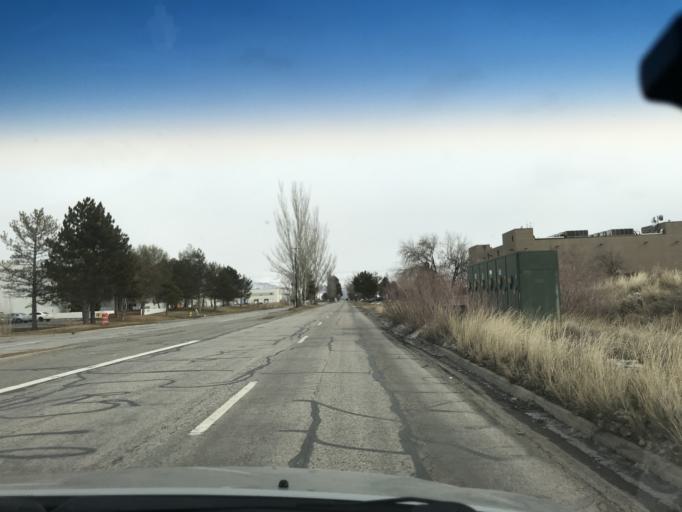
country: US
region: Utah
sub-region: Salt Lake County
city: West Valley City
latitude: 40.7813
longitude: -112.0130
